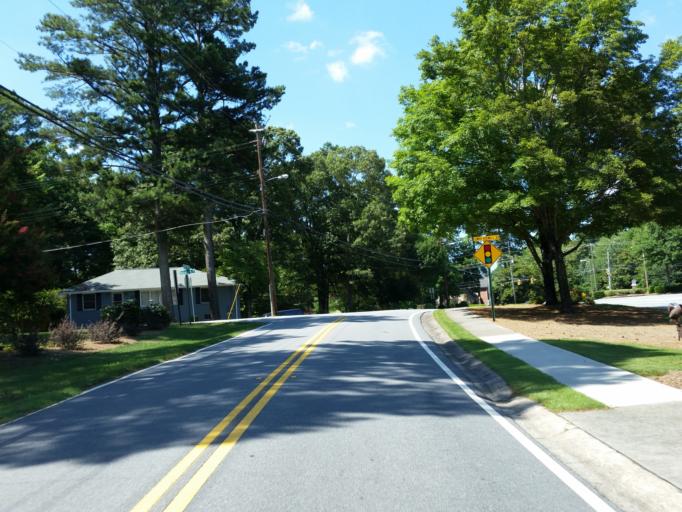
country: US
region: Georgia
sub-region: Cobb County
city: Fair Oaks
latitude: 33.9439
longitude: -84.4829
